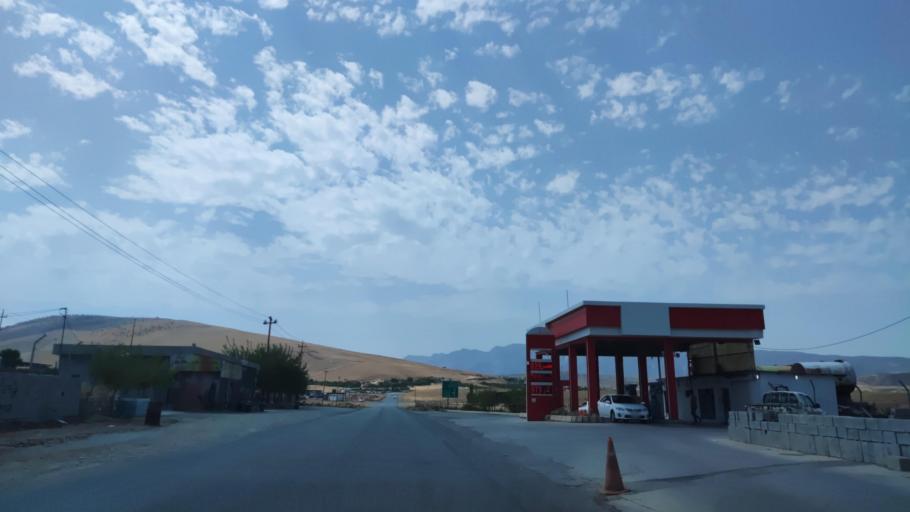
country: IQ
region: Arbil
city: Shaqlawah
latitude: 36.4737
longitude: 44.3975
